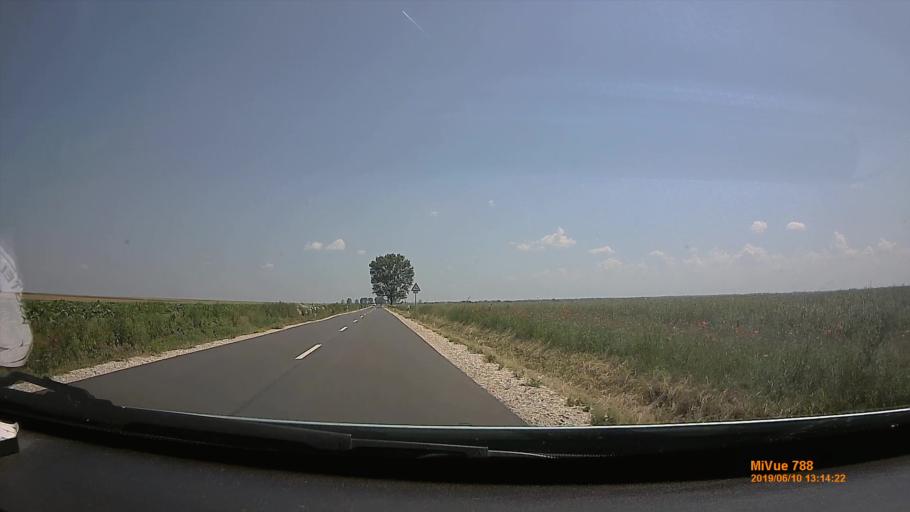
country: HU
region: Borsod-Abauj-Zemplen
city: Hernadnemeti
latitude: 48.0566
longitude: 21.0206
